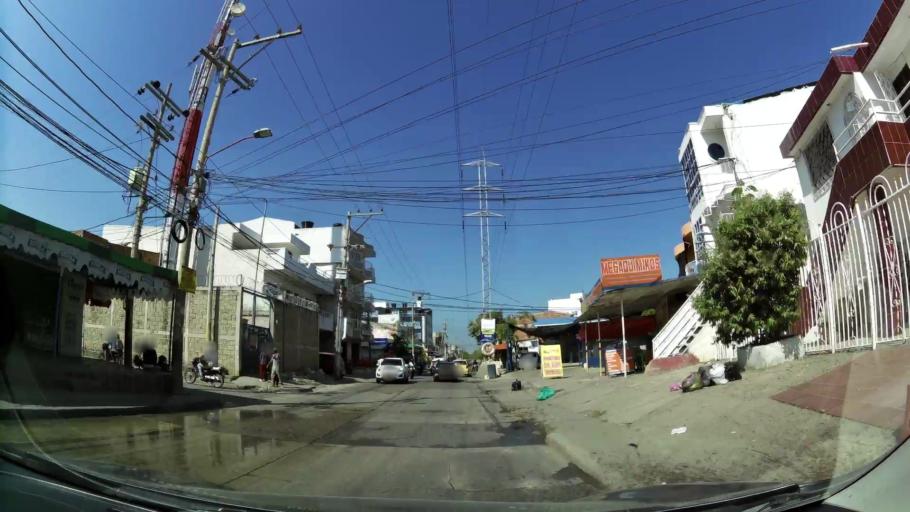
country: CO
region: Bolivar
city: Cartagena
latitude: 10.3790
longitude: -75.4746
